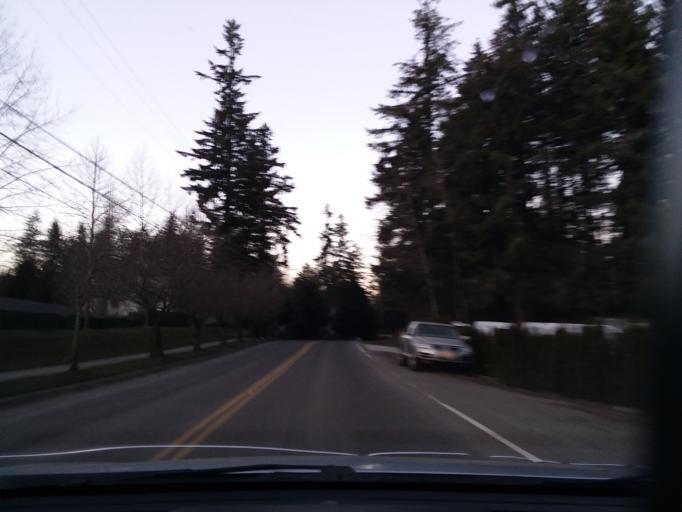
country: US
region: Washington
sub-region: Snohomish County
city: Martha Lake
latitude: 47.8827
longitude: -122.2561
